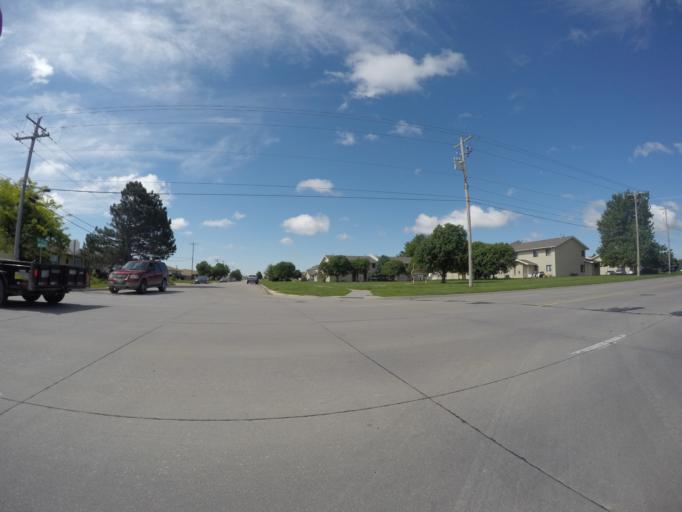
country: US
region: Nebraska
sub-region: Buffalo County
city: Kearney
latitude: 40.6851
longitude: -99.0875
